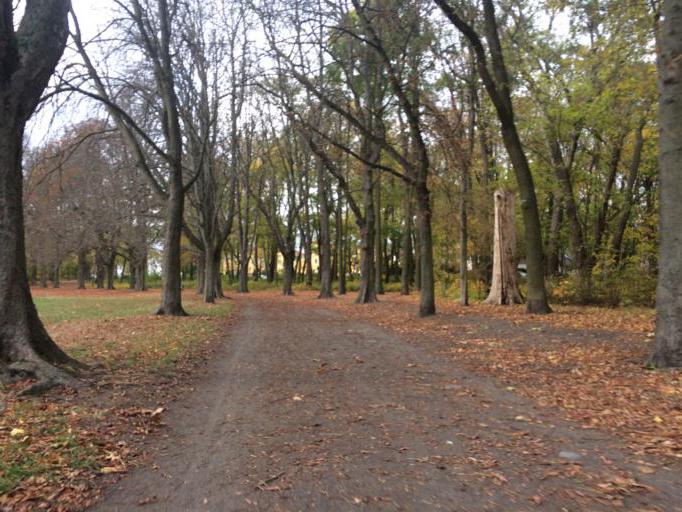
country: DE
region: Berlin
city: Wittenau
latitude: 52.5934
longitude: 13.3181
